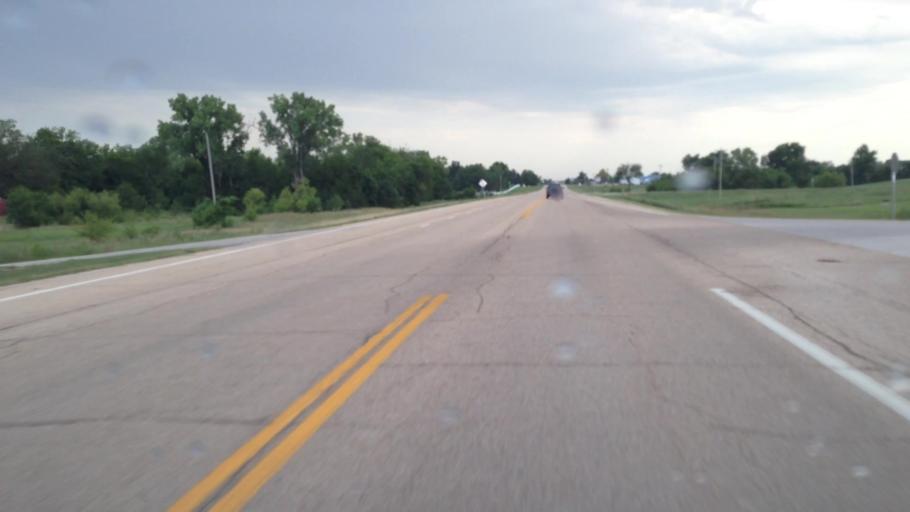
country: US
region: Kansas
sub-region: Coffey County
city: Burlington
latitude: 38.1850
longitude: -95.7387
